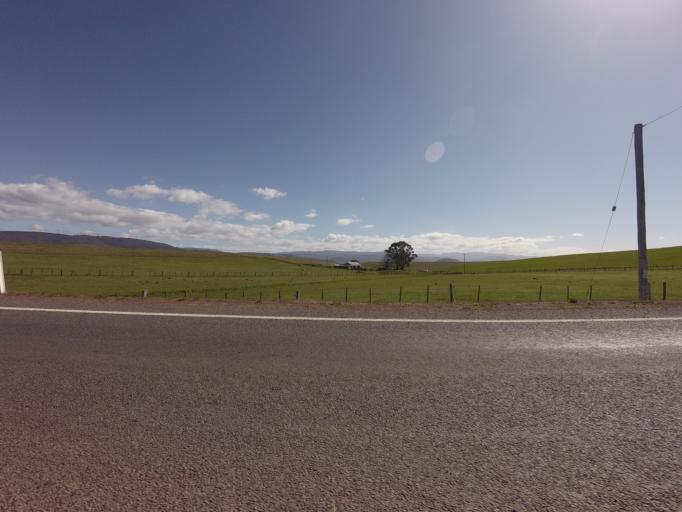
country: AU
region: Tasmania
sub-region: Derwent Valley
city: New Norfolk
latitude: -42.7024
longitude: 146.9420
